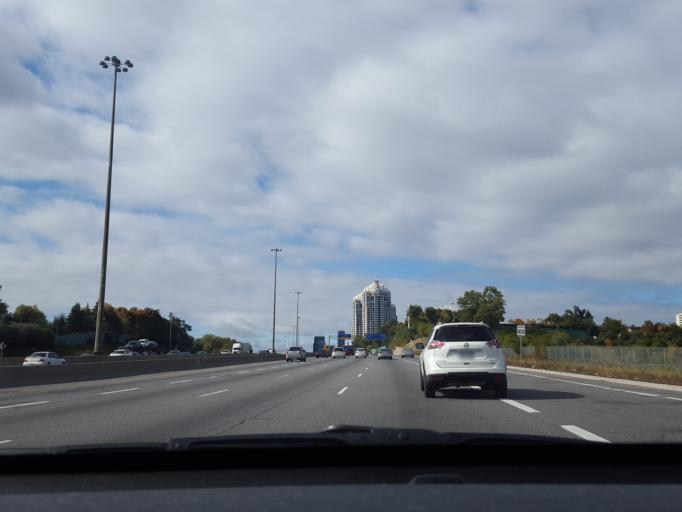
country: CA
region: Ontario
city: Willowdale
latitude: 43.7661
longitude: -79.3722
